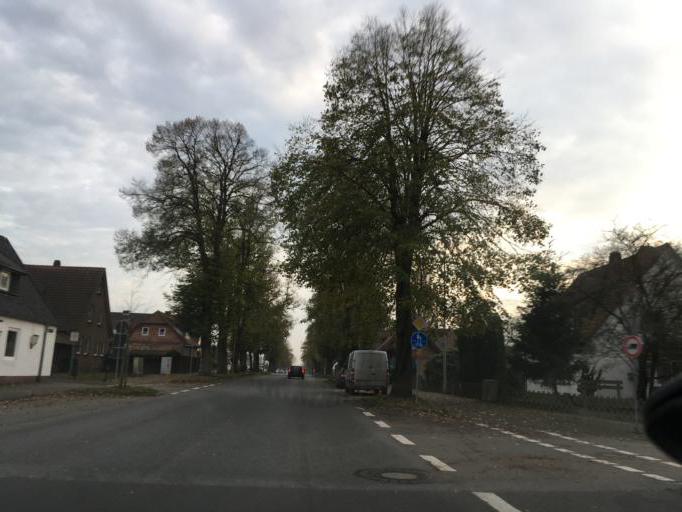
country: DE
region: Lower Saxony
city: Bergen
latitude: 52.8039
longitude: 9.9676
